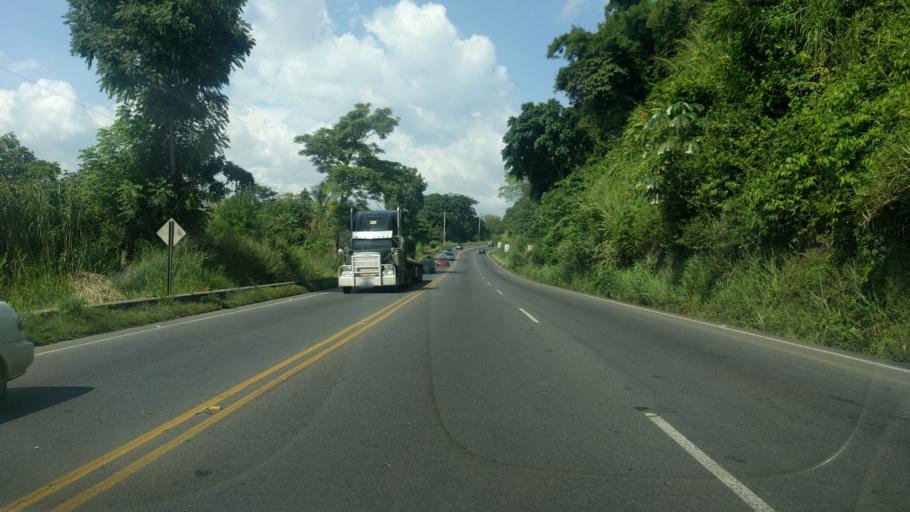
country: CR
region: Alajuela
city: Carrillos
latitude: 10.0039
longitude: -84.2996
